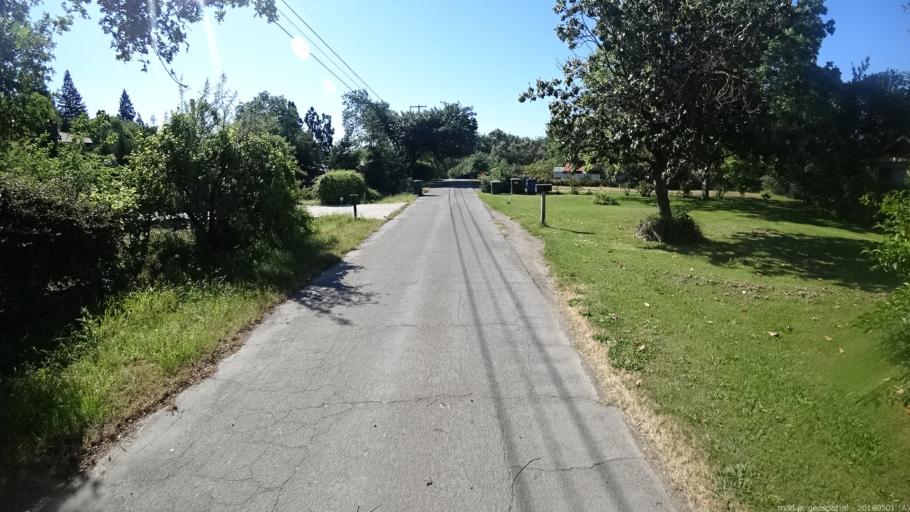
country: US
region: California
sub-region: Sacramento County
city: Arden-Arcade
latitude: 38.6417
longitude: -121.3797
